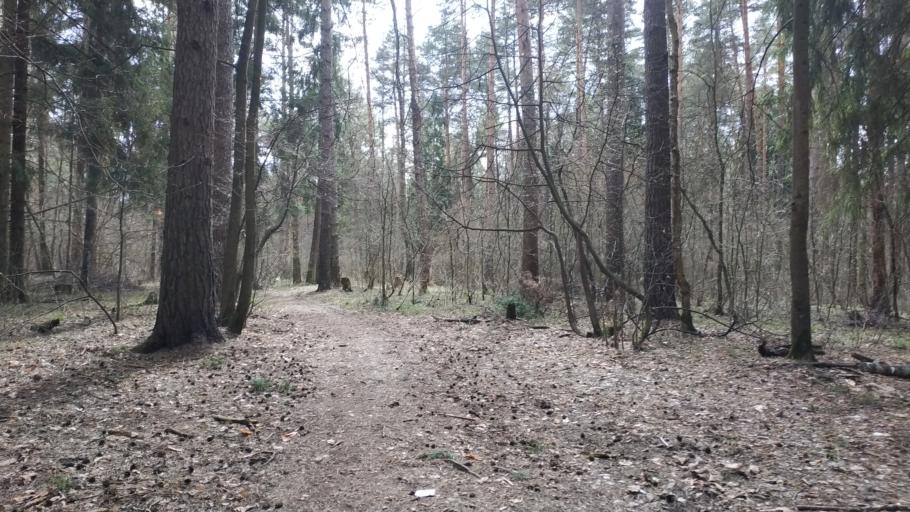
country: RU
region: Moskovskaya
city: Malyshevo
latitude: 55.5477
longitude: 38.3237
